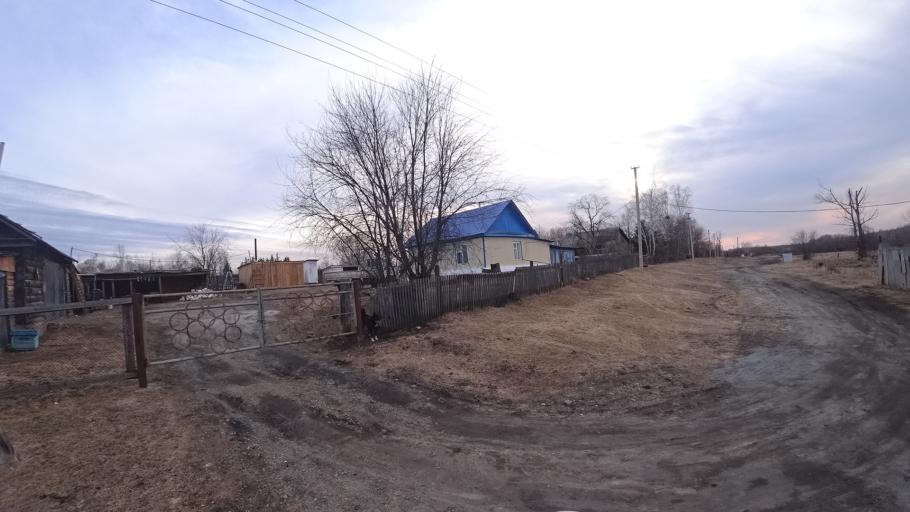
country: RU
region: Amur
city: Bureya
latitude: 50.0215
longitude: 129.7726
